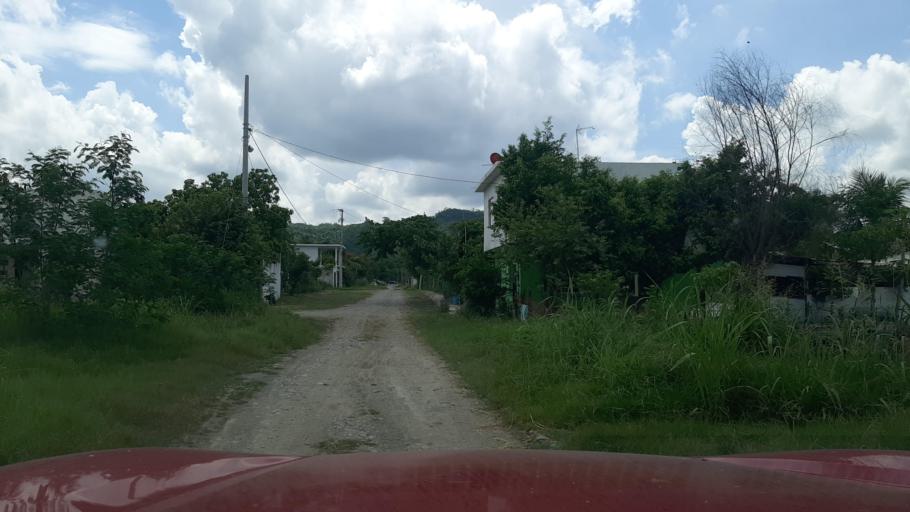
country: MX
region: Veracruz
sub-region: Poza Rica de Hidalgo
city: Villa de las Flores
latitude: 20.5716
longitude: -97.4364
